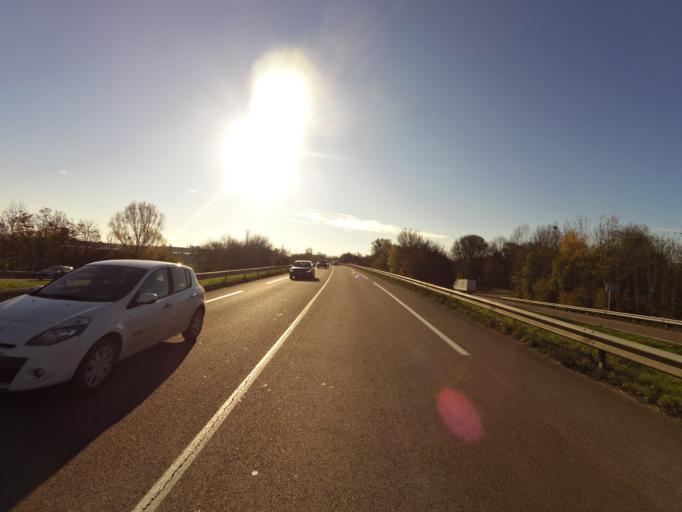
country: FR
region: Champagne-Ardenne
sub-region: Departement de l'Aube
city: Bucheres
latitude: 48.2339
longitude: 4.1236
